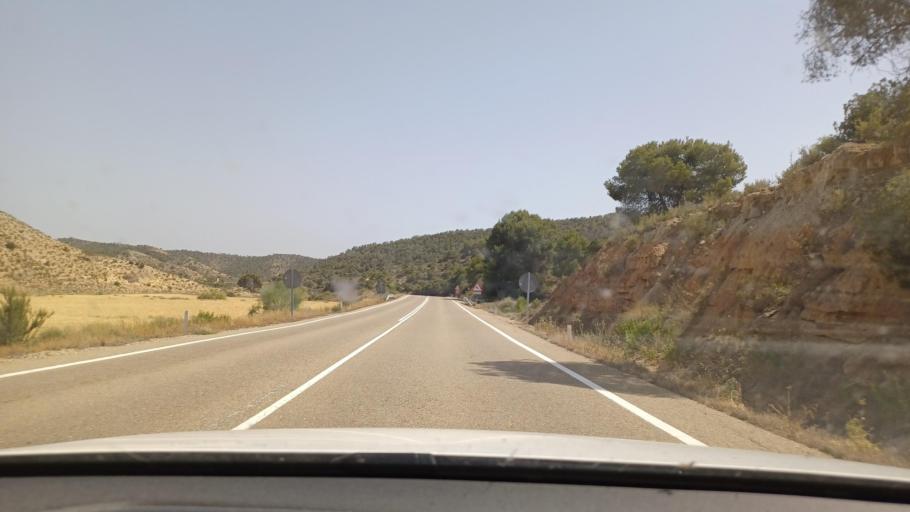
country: ES
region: Aragon
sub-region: Provincia de Zaragoza
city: Chiprana
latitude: 41.3506
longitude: -0.0931
